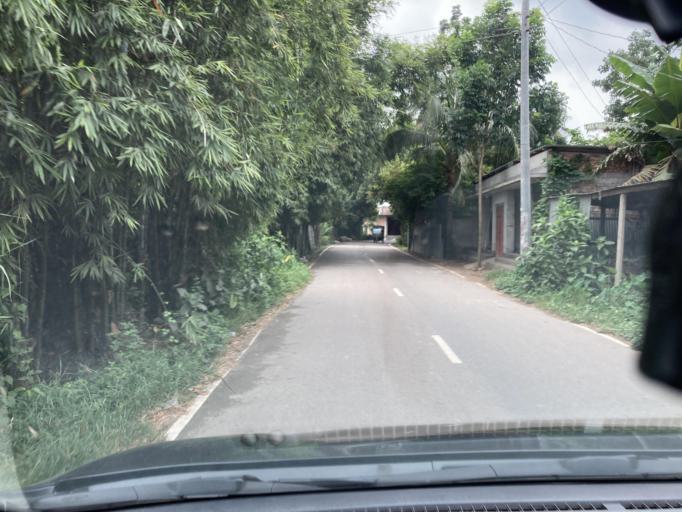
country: BD
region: Dhaka
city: Dohar
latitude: 23.7680
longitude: 90.1970
